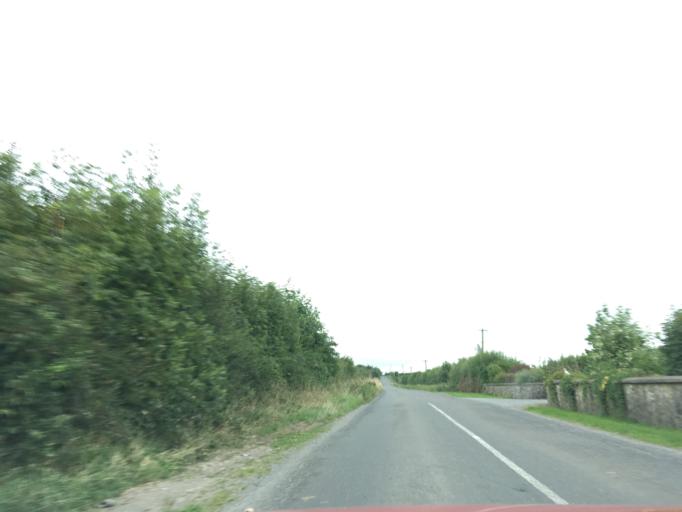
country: IE
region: Munster
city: Cashel
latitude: 52.4735
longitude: -7.8613
